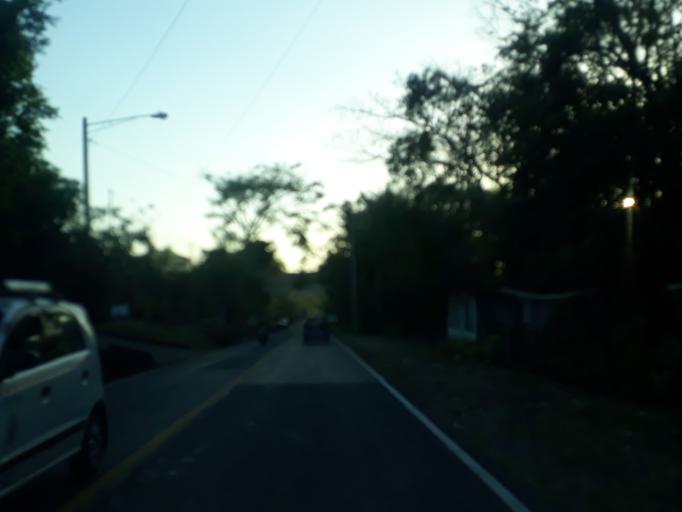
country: NI
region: Masaya
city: Catarina
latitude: 11.9091
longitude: -86.0814
